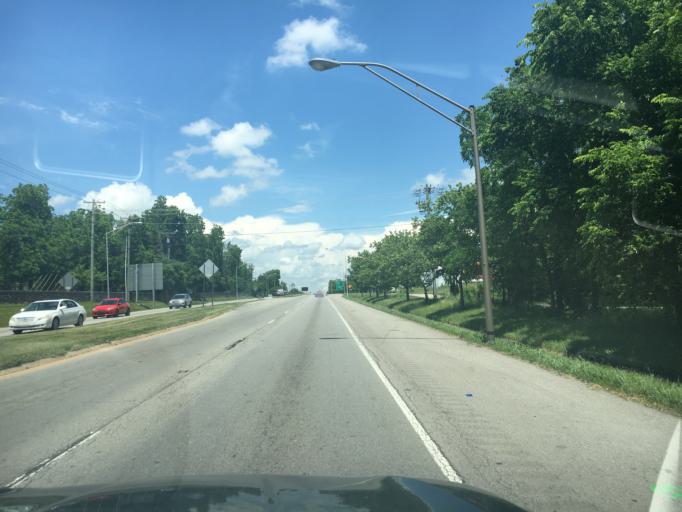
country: US
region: Kentucky
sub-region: Fayette County
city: Lexington-Fayette
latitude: 38.0812
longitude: -84.4922
